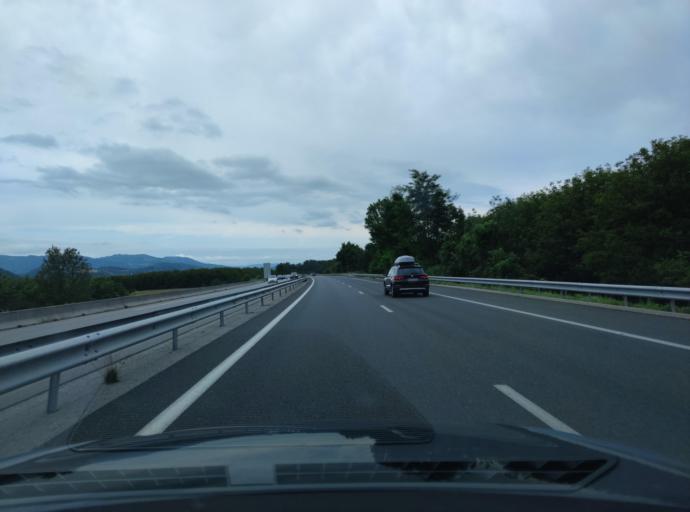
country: FR
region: Rhone-Alpes
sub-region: Departement de l'Isere
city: Vinay
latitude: 45.2234
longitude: 5.4811
